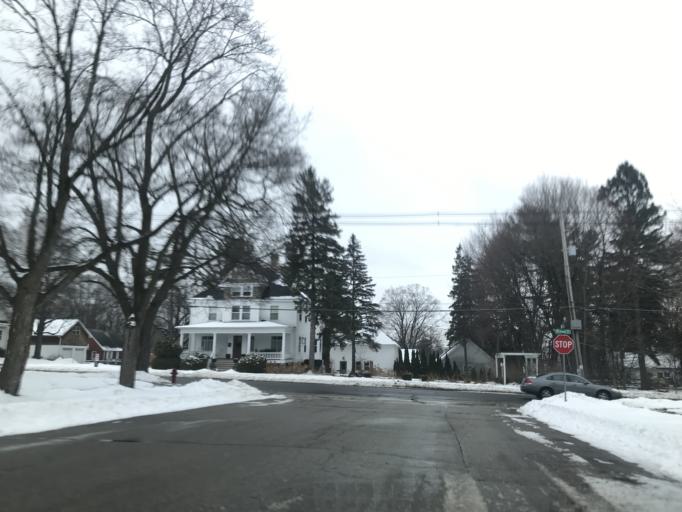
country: US
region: Wisconsin
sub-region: Door County
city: Sturgeon Bay
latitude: 44.8355
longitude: -87.3710
